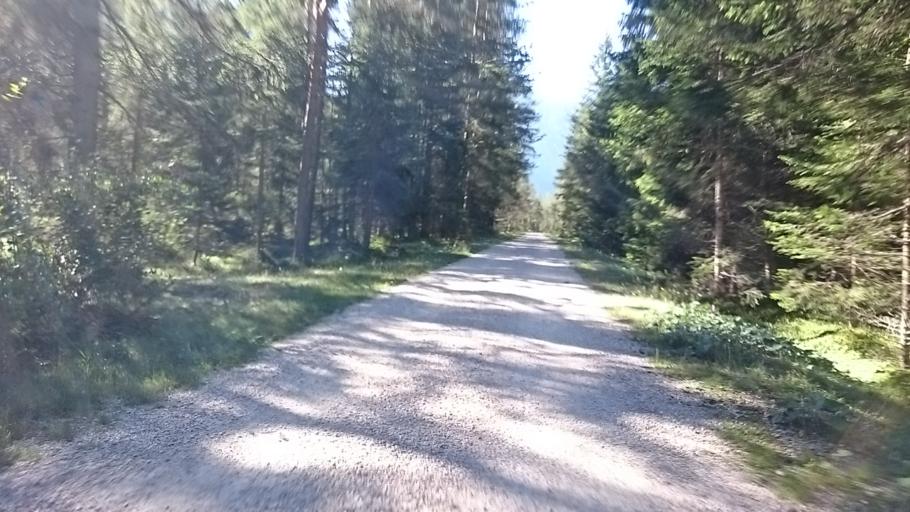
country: IT
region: Trentino-Alto Adige
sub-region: Bolzano
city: Dobbiaco
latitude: 46.6548
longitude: 12.2261
